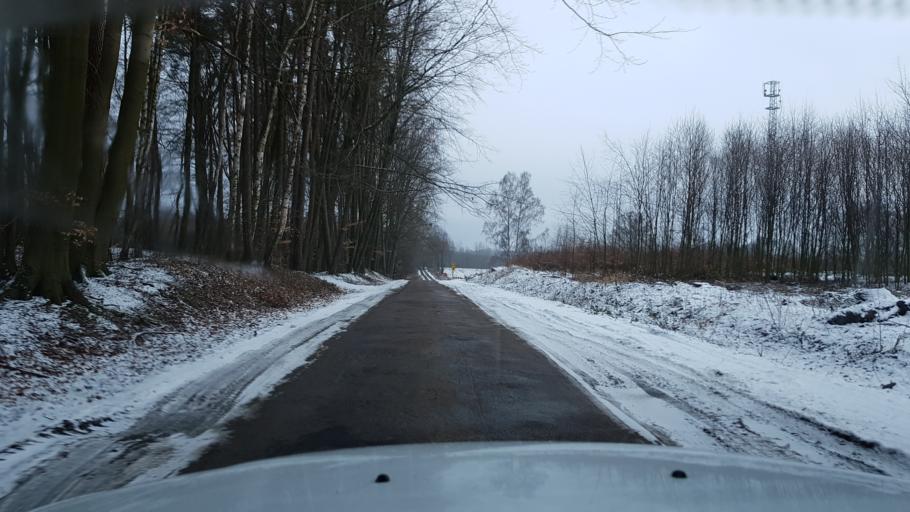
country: PL
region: West Pomeranian Voivodeship
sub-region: Powiat drawski
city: Zlocieniec
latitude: 53.5316
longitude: 16.0805
